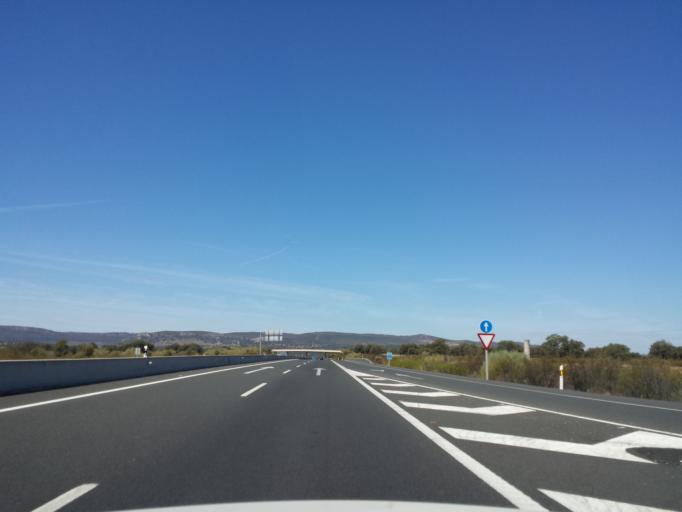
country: ES
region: Extremadura
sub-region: Provincia de Caceres
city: Almaraz
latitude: 39.7895
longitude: -5.7038
